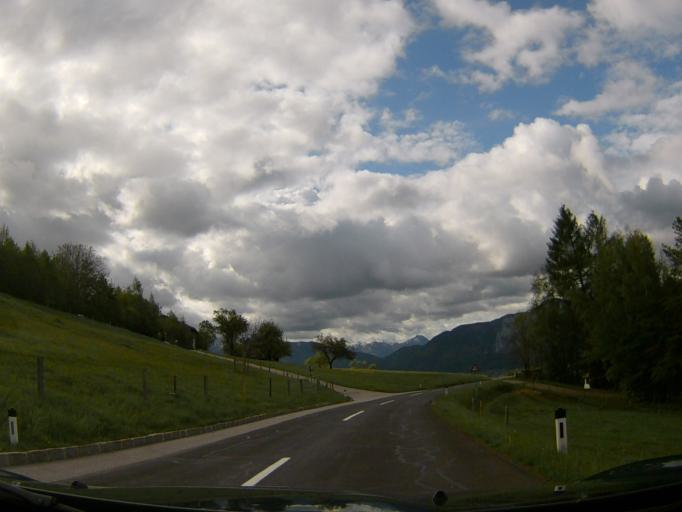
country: AT
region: Upper Austria
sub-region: Politischer Bezirk Vocklabruck
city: Mondsee
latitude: 47.8694
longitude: 13.3520
